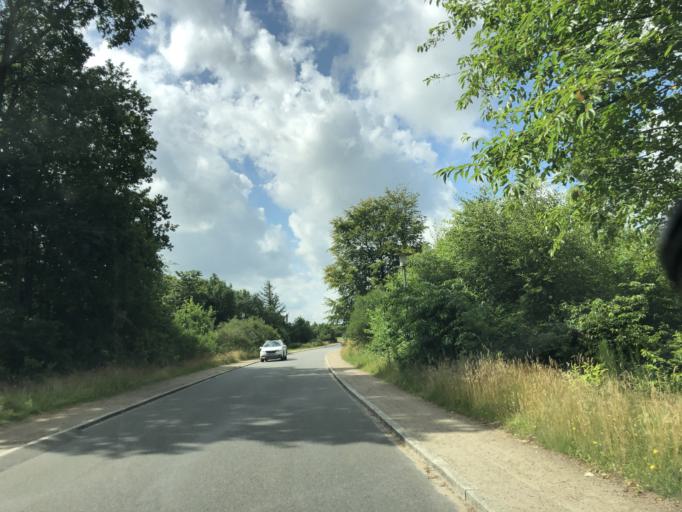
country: DK
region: Central Jutland
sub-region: Ikast-Brande Kommune
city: Brande
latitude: 55.9371
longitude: 9.1508
